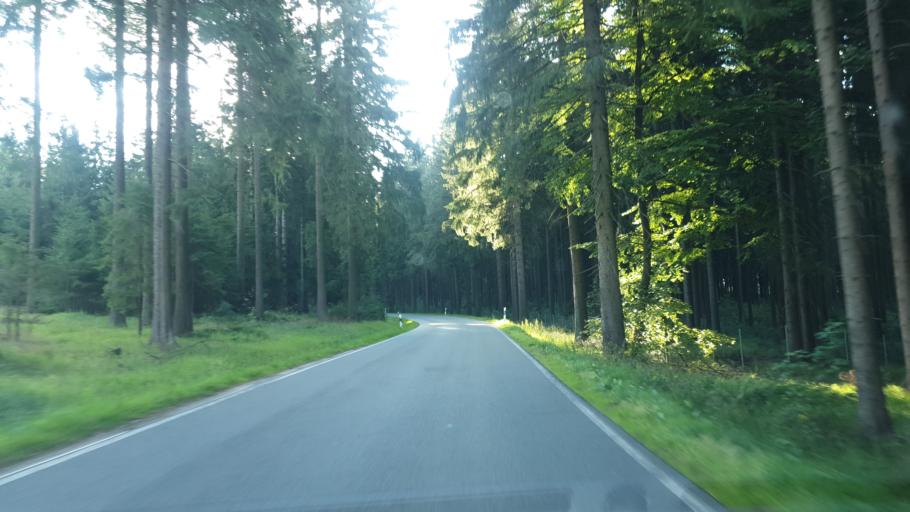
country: DE
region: Saxony
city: Tannenbergsthal
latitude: 50.4371
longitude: 12.4419
